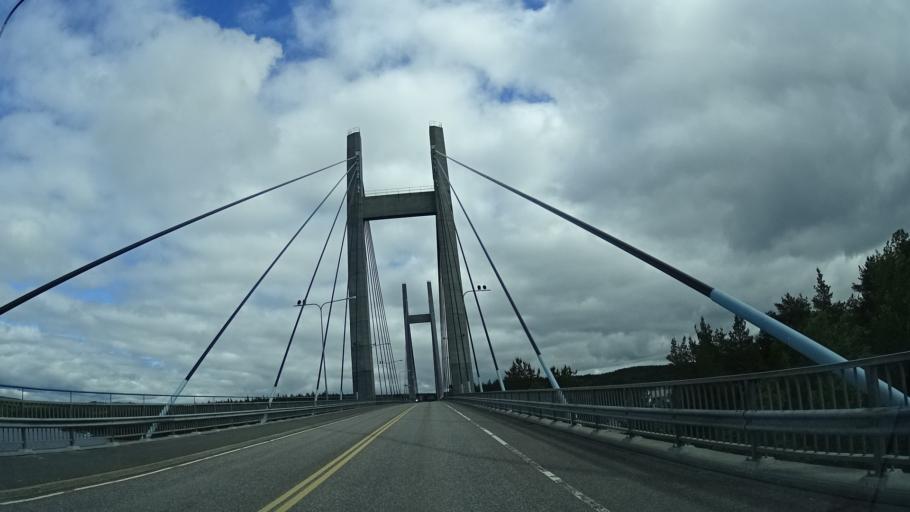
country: FI
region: Central Finland
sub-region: Jyvaeskylae
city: Korpilahti
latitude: 61.9964
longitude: 25.6741
